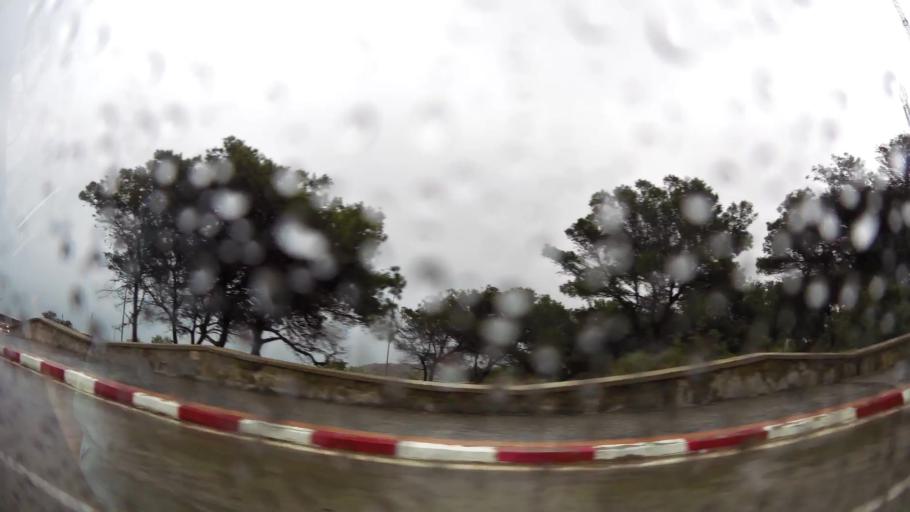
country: MA
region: Taza-Al Hoceima-Taounate
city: Al Hoceima
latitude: 35.2501
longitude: -3.9442
